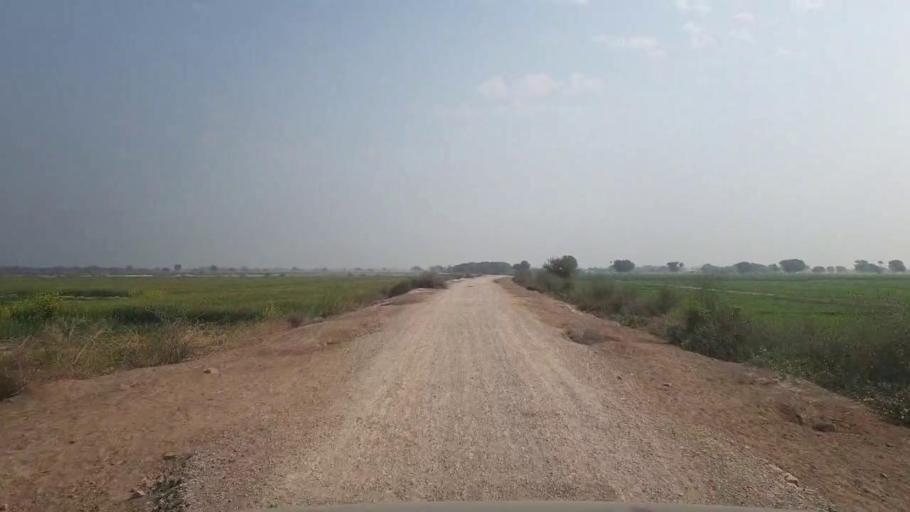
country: PK
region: Sindh
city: Hala
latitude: 25.7643
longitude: 68.4207
